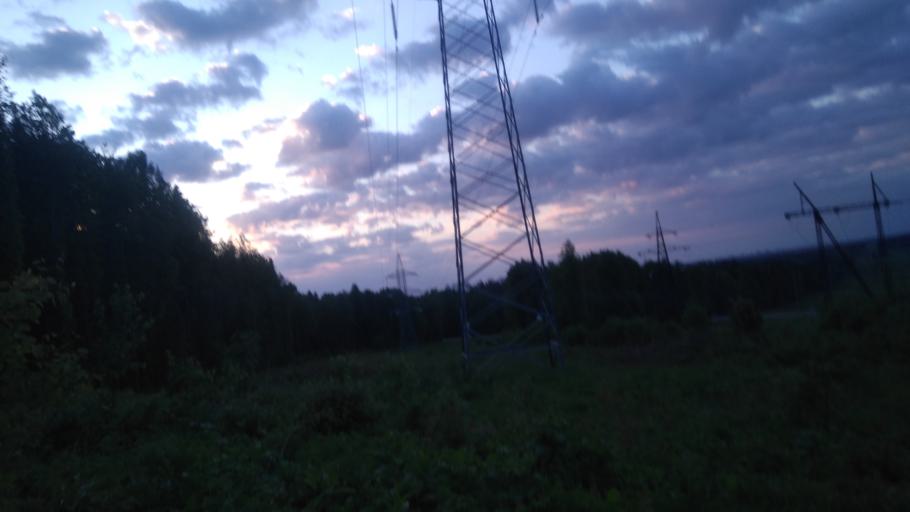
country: RU
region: Perm
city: Ferma
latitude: 57.9707
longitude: 56.3444
